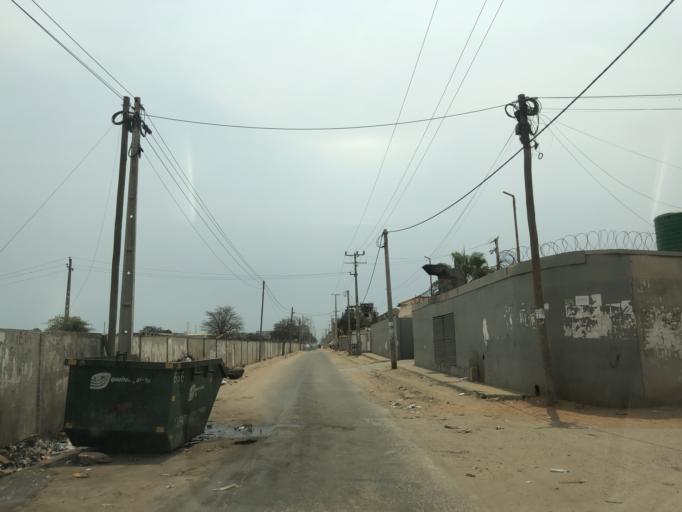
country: AO
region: Luanda
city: Luanda
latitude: -8.8884
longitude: 13.1934
